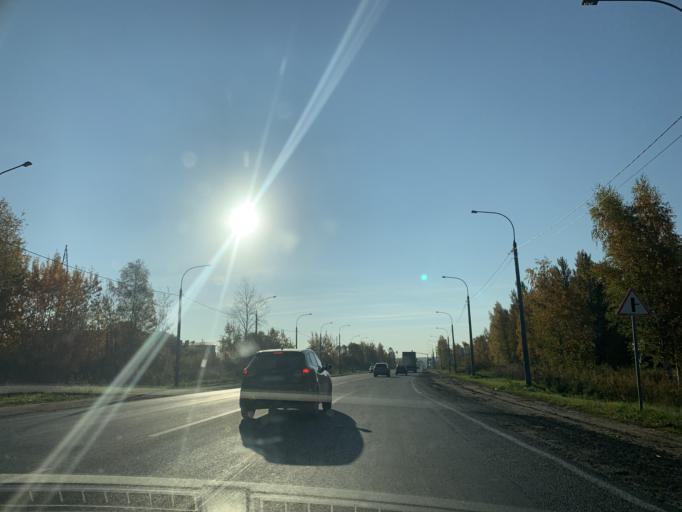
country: RU
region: Jaroslavl
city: Yaroslavl
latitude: 57.6161
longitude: 39.7812
